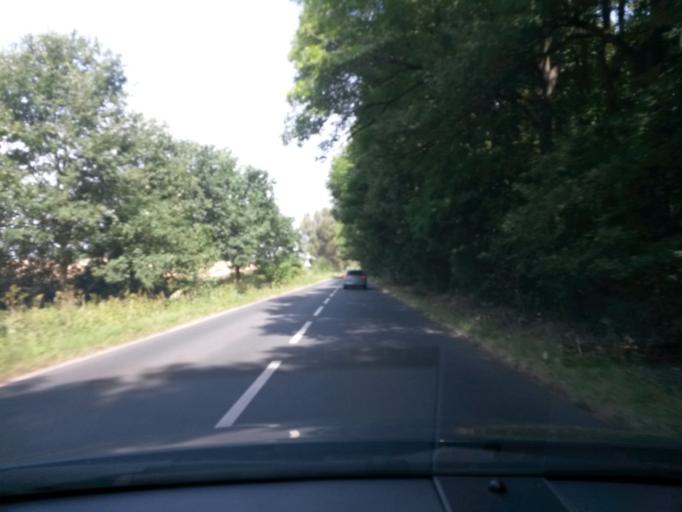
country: PL
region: Lower Silesian Voivodeship
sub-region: Powiat legnicki
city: Legnickie Pole
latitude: 51.1615
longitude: 16.3360
